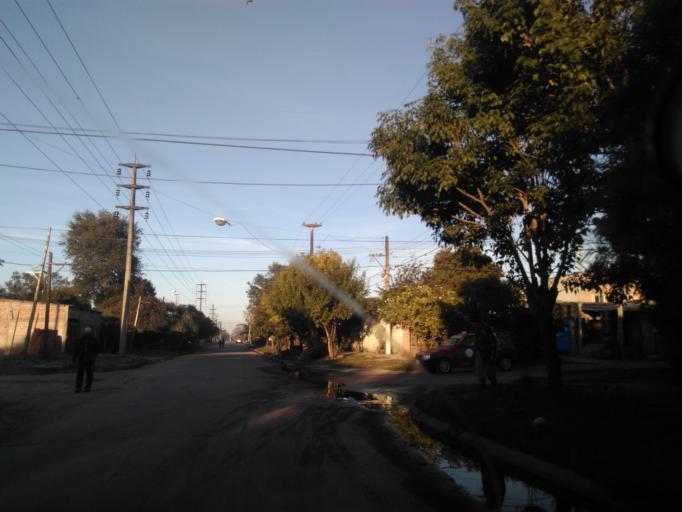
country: AR
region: Chaco
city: Resistencia
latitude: -27.4710
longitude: -59.0034
